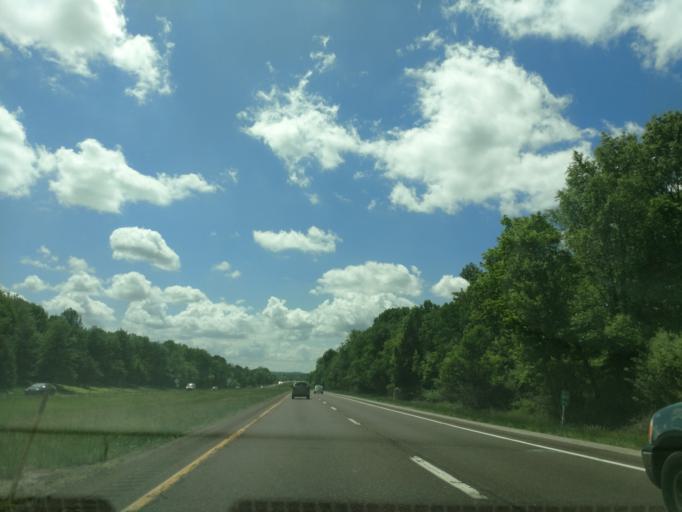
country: US
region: Pennsylvania
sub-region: Montgomery County
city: Audubon
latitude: 40.1157
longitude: -75.4321
